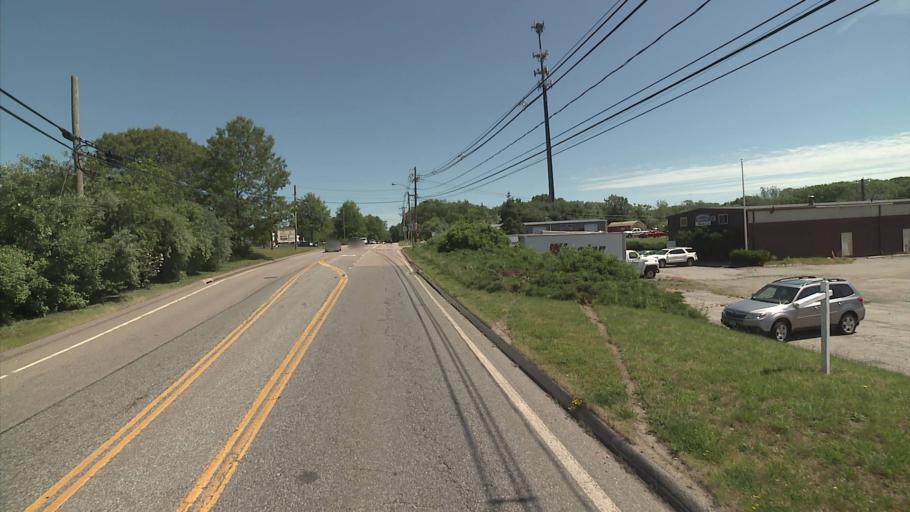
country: US
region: Connecticut
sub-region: New London County
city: Pawcatuck
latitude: 41.4047
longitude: -71.8462
